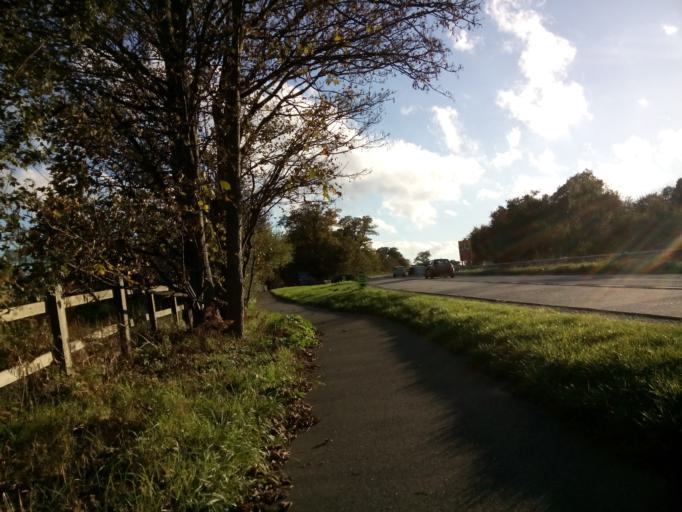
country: GB
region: England
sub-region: Suffolk
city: Kesgrave
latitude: 52.0529
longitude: 1.2781
